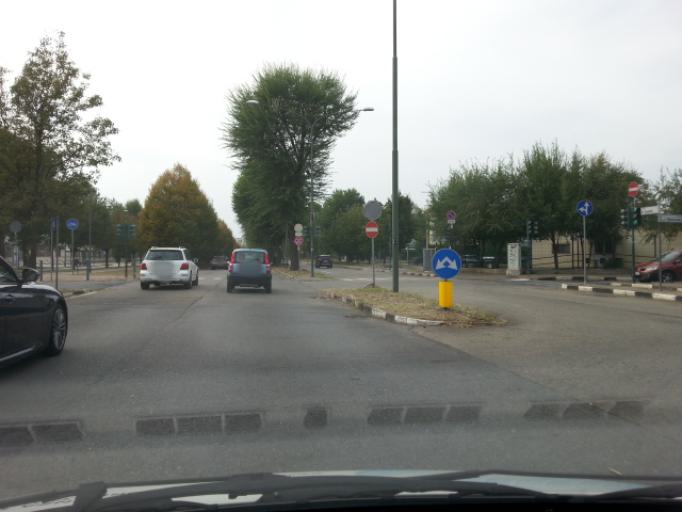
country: IT
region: Piedmont
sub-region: Provincia di Torino
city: Gerbido
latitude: 45.0326
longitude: 7.6341
